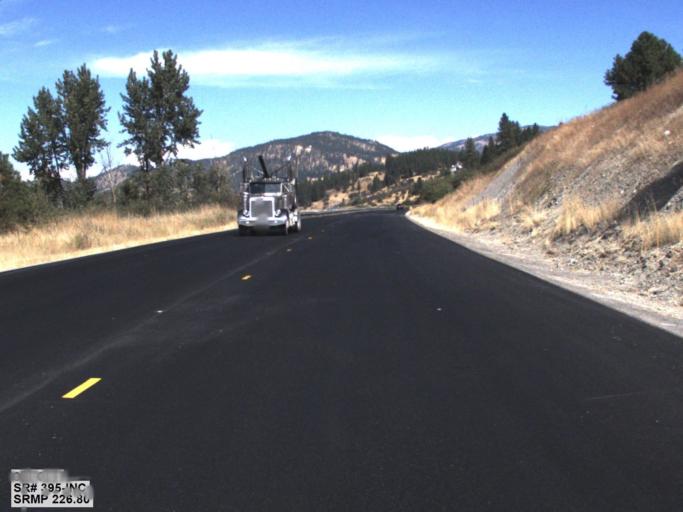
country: US
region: Washington
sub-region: Stevens County
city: Colville
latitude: 48.5056
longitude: -117.9021
